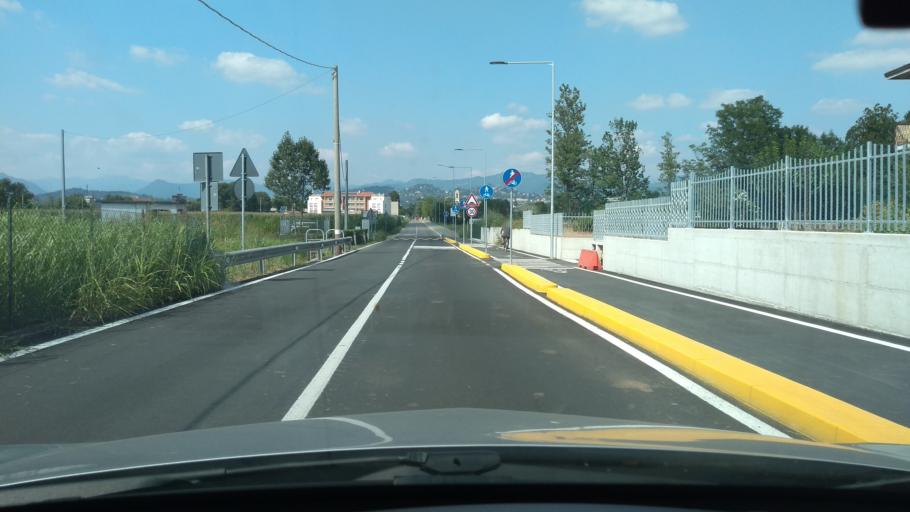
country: IT
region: Lombardy
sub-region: Provincia di Bergamo
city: Lallio
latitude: 45.6619
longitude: 9.6392
